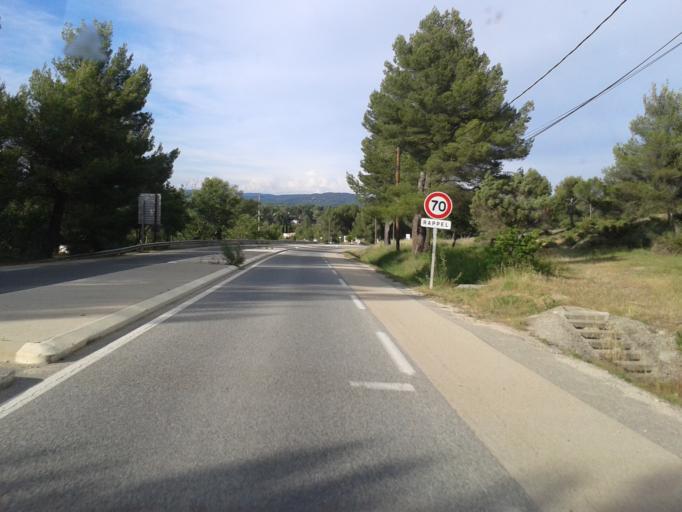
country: FR
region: Provence-Alpes-Cote d'Azur
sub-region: Departement des Bouches-du-Rhone
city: Meyrargues
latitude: 43.6309
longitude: 5.5128
